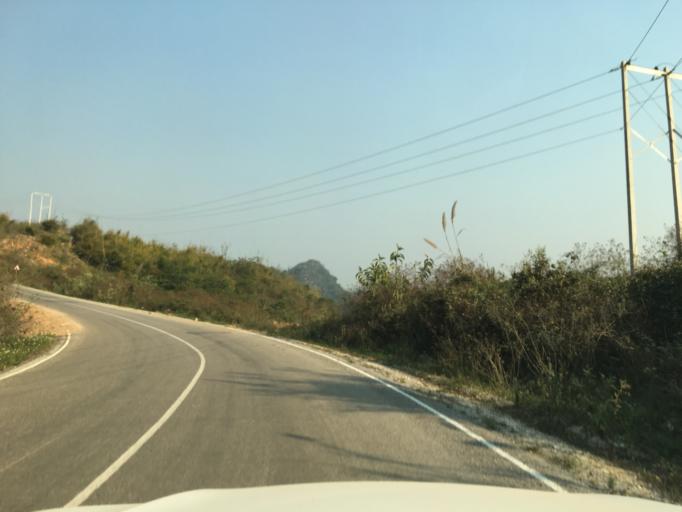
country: LA
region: Houaphan
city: Xam Nua
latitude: 20.5673
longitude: 104.0578
